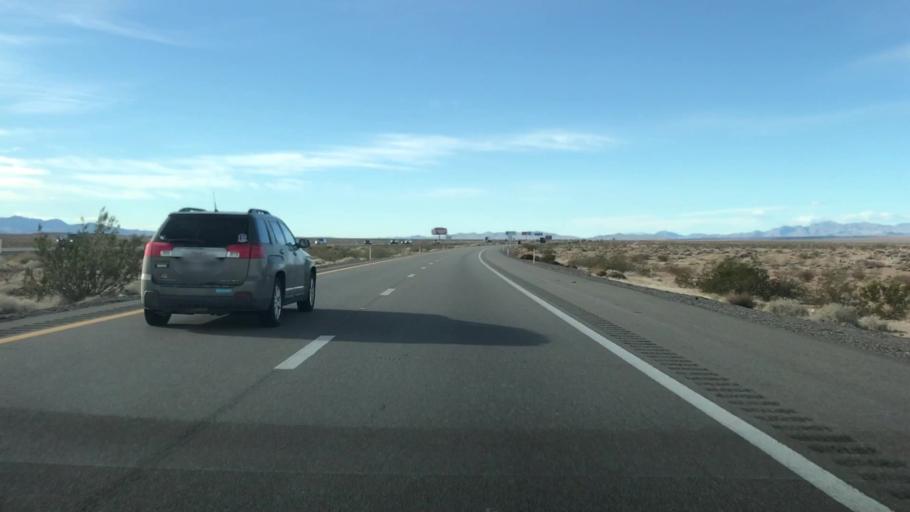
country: US
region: Nevada
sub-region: Clark County
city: Moapa Town
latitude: 36.5830
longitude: -114.6533
